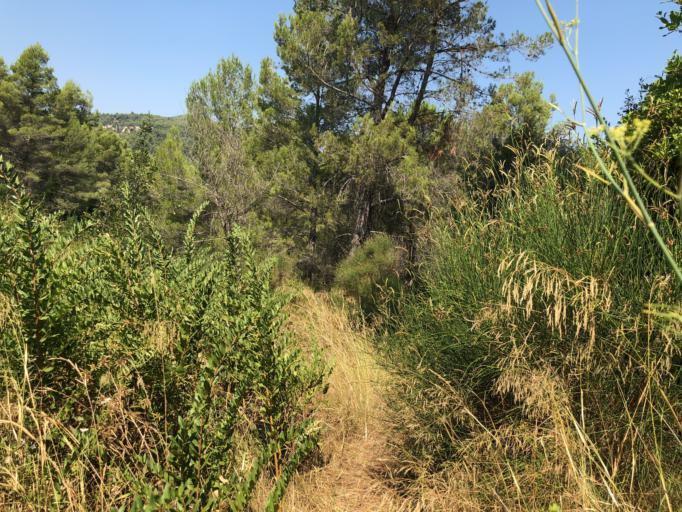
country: ES
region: Catalonia
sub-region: Provincia de Barcelona
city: Corbera de Llobregat
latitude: 41.4170
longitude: 1.9116
